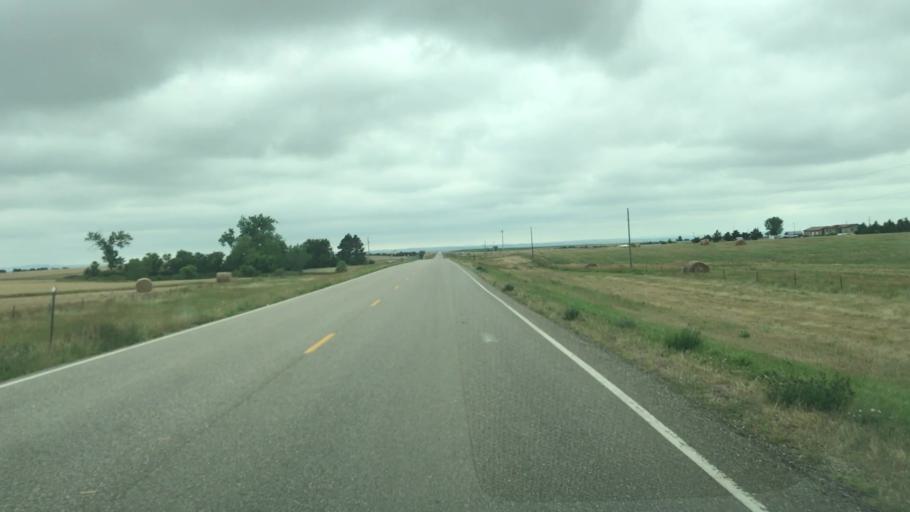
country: US
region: South Dakota
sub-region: Jackson County
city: Kadoka
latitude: 43.8312
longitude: -101.5225
